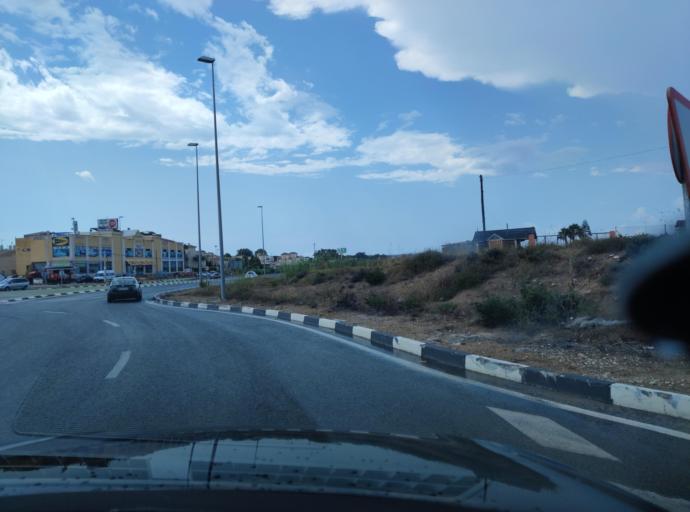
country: ES
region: Valencia
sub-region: Provincia de Alicante
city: Guardamar del Segura
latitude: 38.0493
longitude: -0.6587
